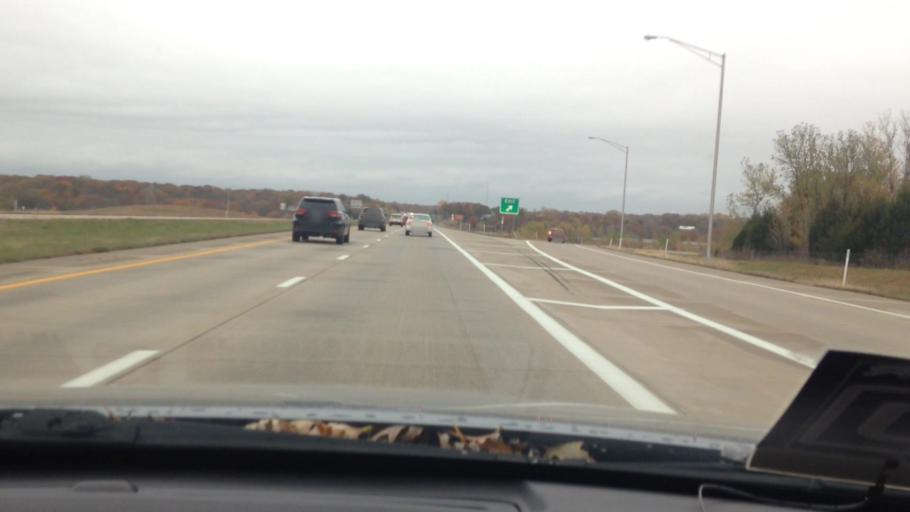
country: US
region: Kansas
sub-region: Leavenworth County
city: Basehor
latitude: 39.1195
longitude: -94.8991
